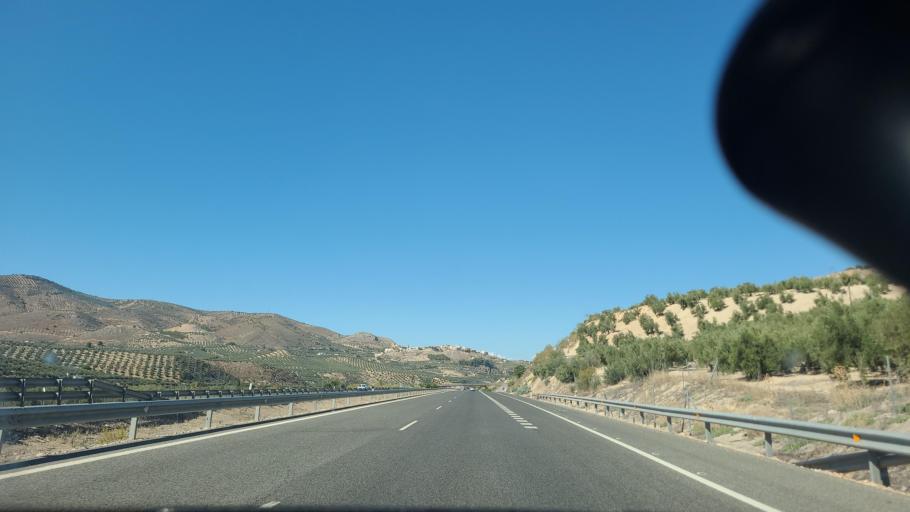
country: ES
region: Andalusia
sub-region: Provincia de Jaen
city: La Guardia de Jaen
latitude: 37.7203
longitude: -3.6760
